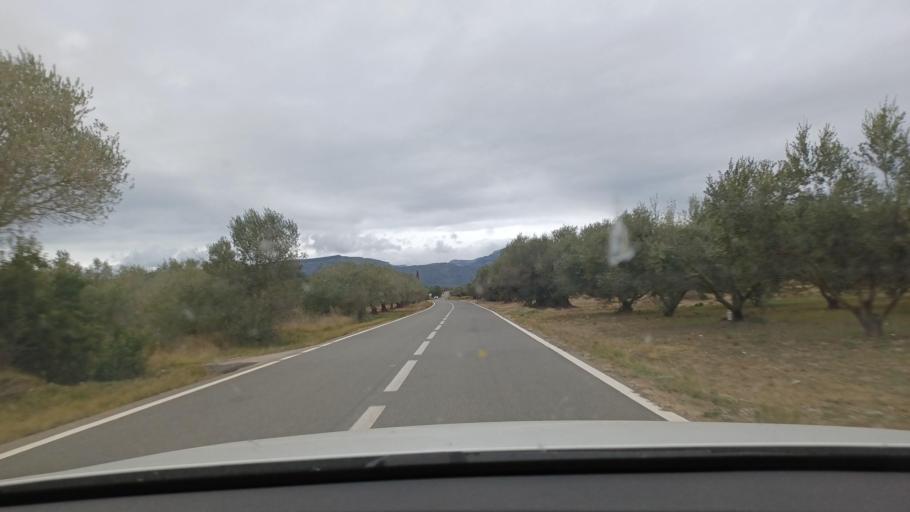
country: ES
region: Catalonia
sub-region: Provincia de Tarragona
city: Ulldecona
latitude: 40.6357
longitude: 0.3580
